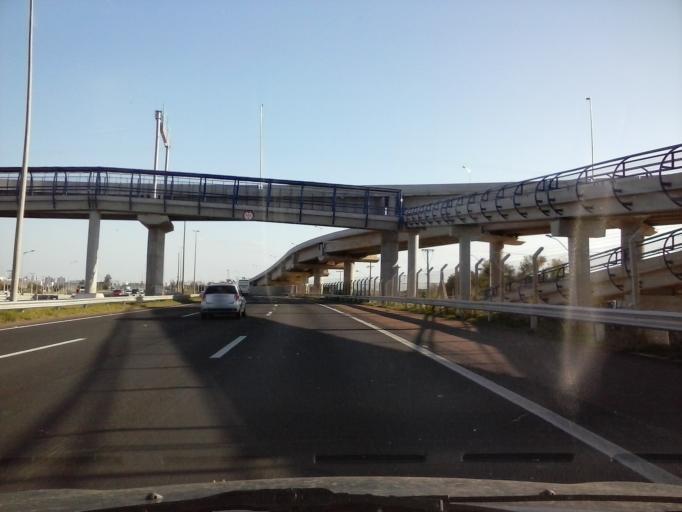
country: BR
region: Rio Grande do Sul
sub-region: Canoas
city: Canoas
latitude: -29.9743
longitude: -51.1987
